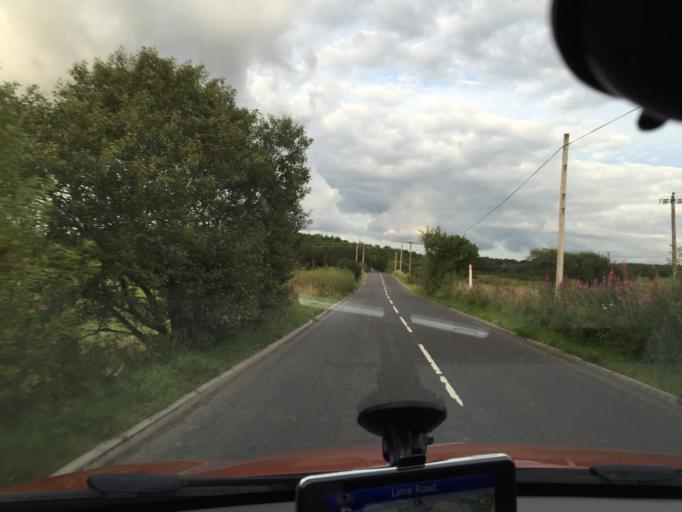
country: GB
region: Scotland
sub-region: Falkirk
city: Bonnybridge
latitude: 55.9929
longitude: -3.8655
